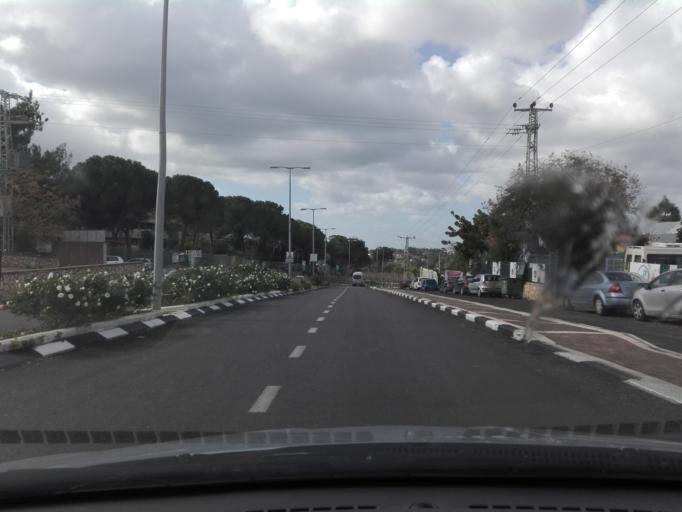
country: IL
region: Haifa
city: Daliyat el Karmil
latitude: 32.7060
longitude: 35.0610
